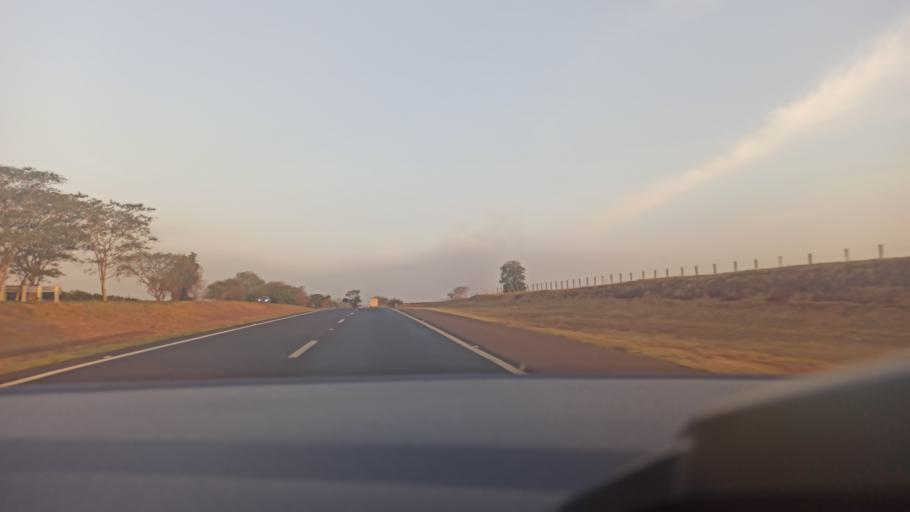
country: BR
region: Sao Paulo
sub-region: Taquaritinga
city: Taquaritinga
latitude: -21.4388
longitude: -48.6520
